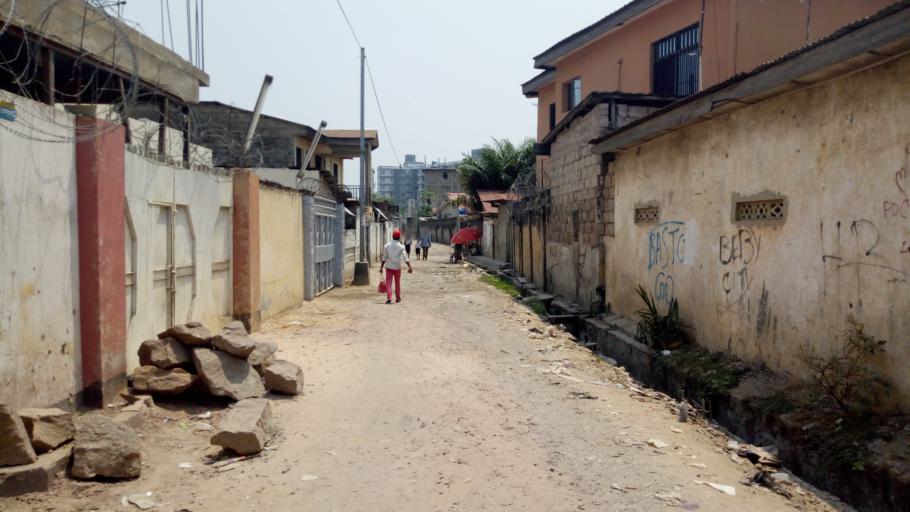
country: CD
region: Kinshasa
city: Kinshasa
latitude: -4.3163
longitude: 15.2941
